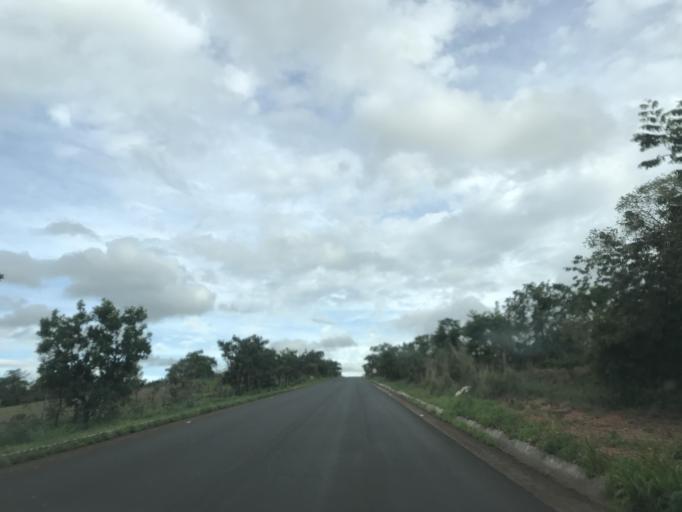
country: BR
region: Goias
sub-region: Vianopolis
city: Vianopolis
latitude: -16.9475
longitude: -48.5771
